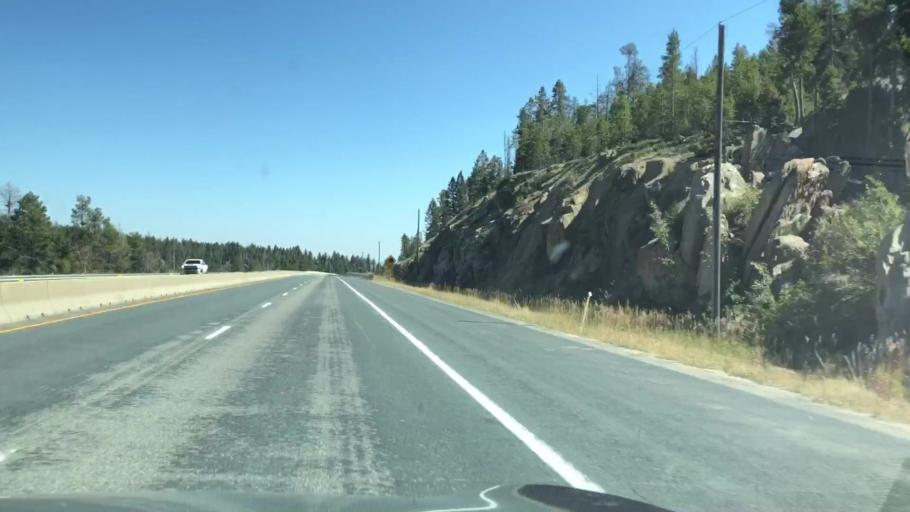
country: US
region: Montana
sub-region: Silver Bow County
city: Butte
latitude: 45.9144
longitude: -112.3642
